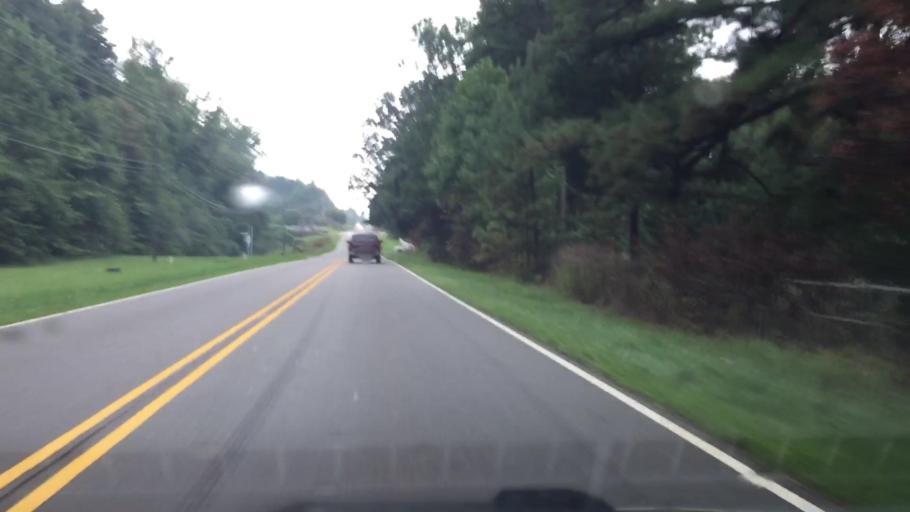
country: US
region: North Carolina
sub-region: Iredell County
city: Mooresville
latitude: 35.5678
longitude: -80.8465
